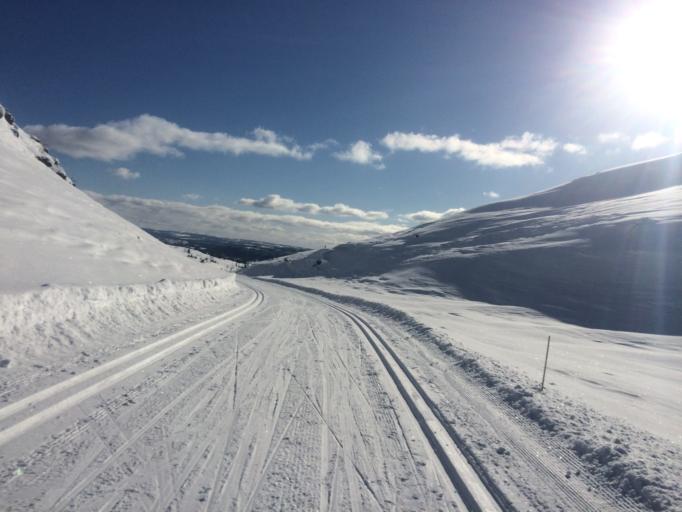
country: NO
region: Oppland
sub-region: Ringebu
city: Ringebu
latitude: 61.3772
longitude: 10.0593
